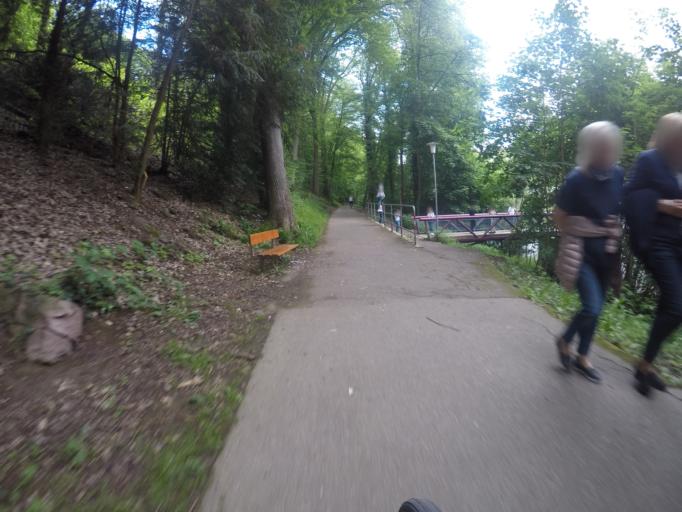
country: DE
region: Baden-Wuerttemberg
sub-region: Karlsruhe Region
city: Pforzheim
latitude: 48.8743
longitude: 8.6754
